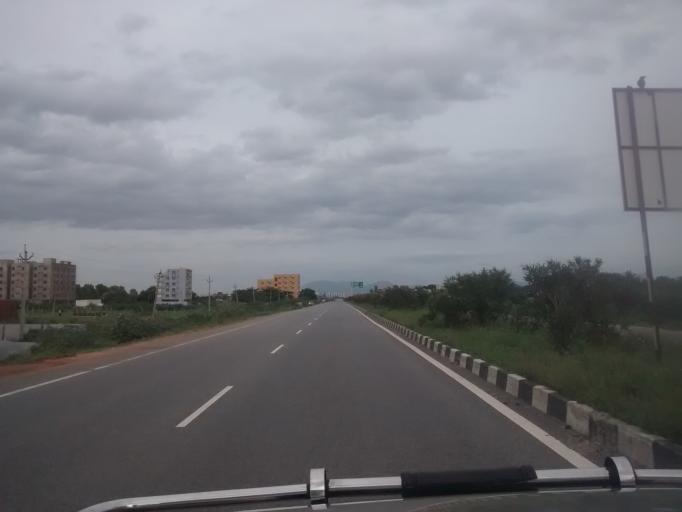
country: IN
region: Andhra Pradesh
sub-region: Chittoor
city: Tirupati
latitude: 13.6045
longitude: 79.3910
